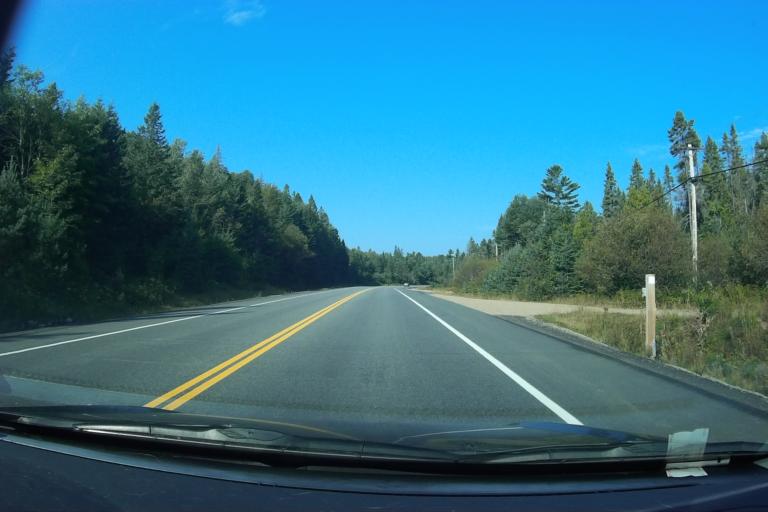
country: CA
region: Ontario
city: Huntsville
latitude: 45.5526
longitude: -78.6114
